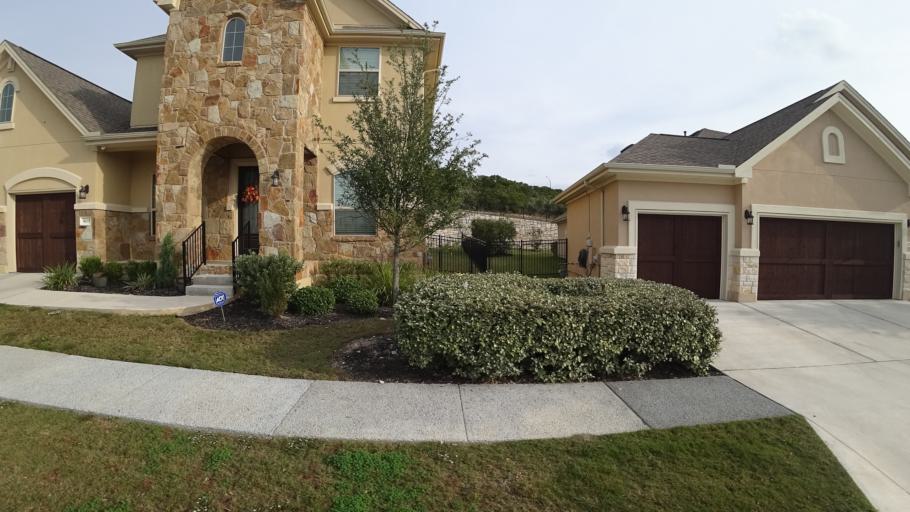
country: US
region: Texas
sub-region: Travis County
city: Hudson Bend
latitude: 30.3787
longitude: -97.8819
